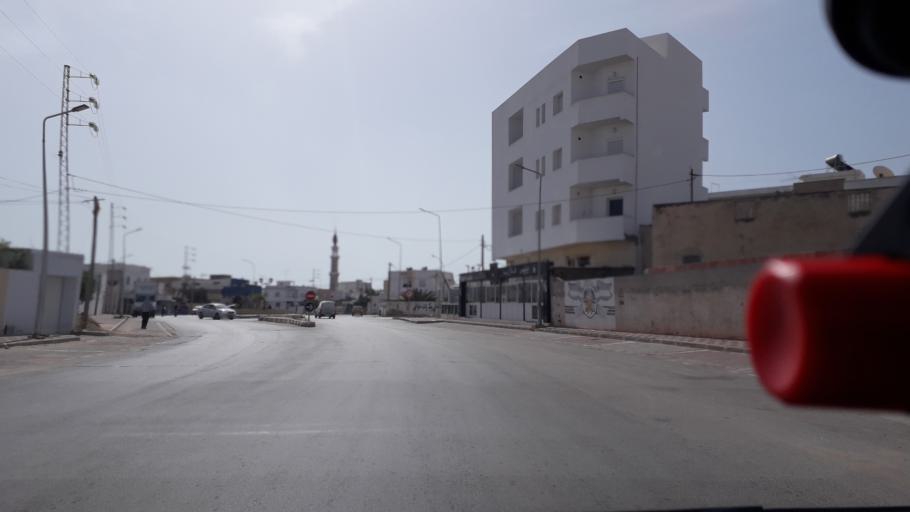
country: TN
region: Safaqis
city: Al Qarmadah
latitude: 34.8014
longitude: 10.7629
